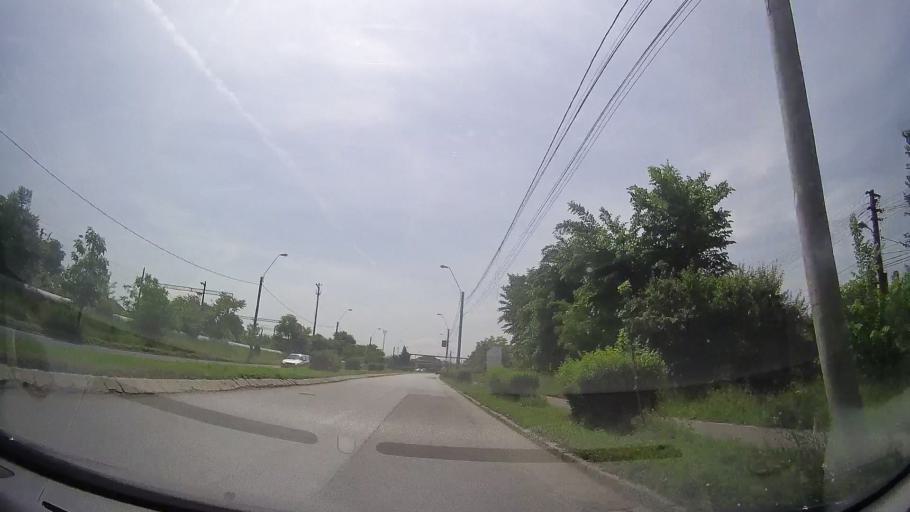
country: RO
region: Hunedoara
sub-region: Municipiul Deva
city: Deva
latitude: 45.8901
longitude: 22.9059
